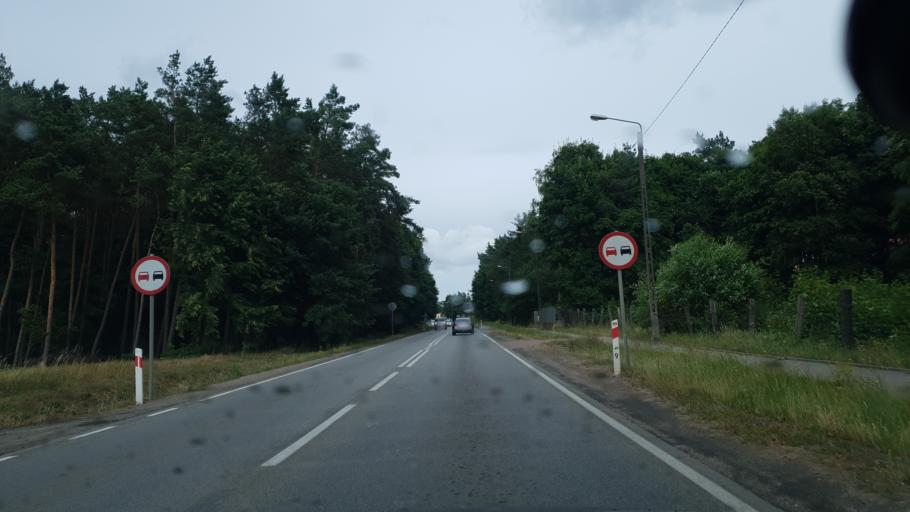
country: PL
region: Pomeranian Voivodeship
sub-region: Powiat kartuski
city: Chwaszczyno
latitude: 54.4380
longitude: 18.4103
